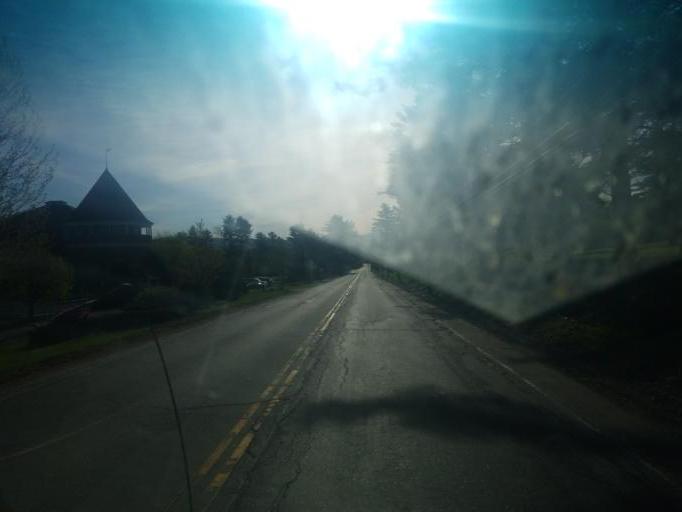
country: US
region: New Hampshire
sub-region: Grafton County
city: Deerfield
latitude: 44.2817
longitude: -71.6661
